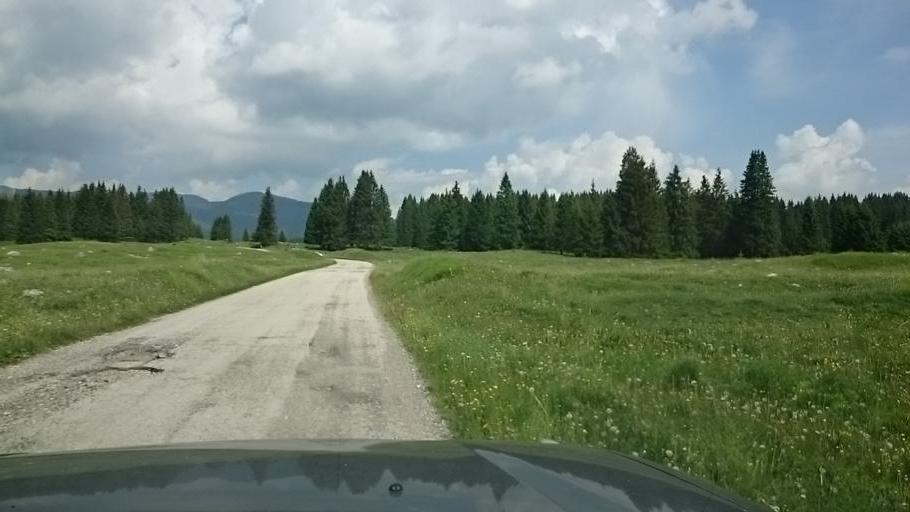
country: IT
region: Trentino-Alto Adige
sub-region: Provincia di Trento
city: Grigno
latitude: 45.9691
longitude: 11.6023
